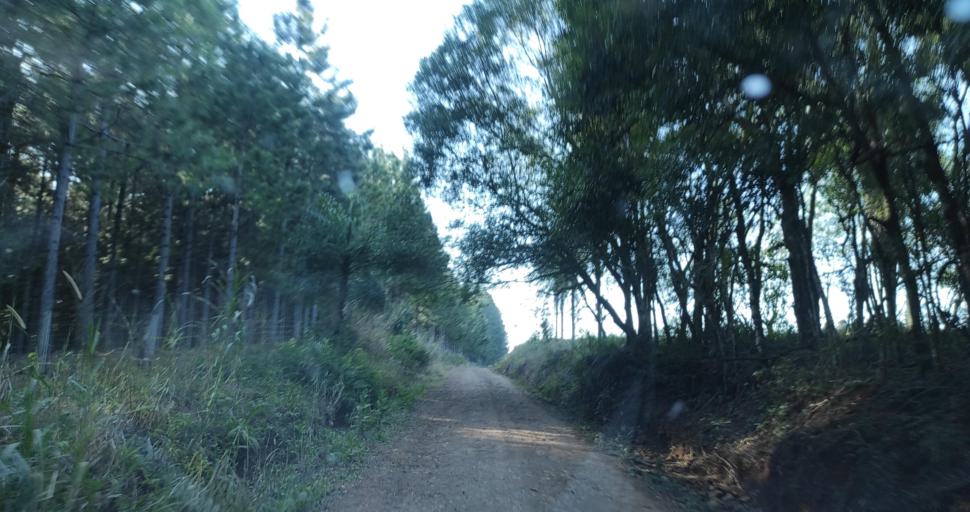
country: AR
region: Misiones
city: Capiovi
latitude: -26.8920
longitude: -55.1072
